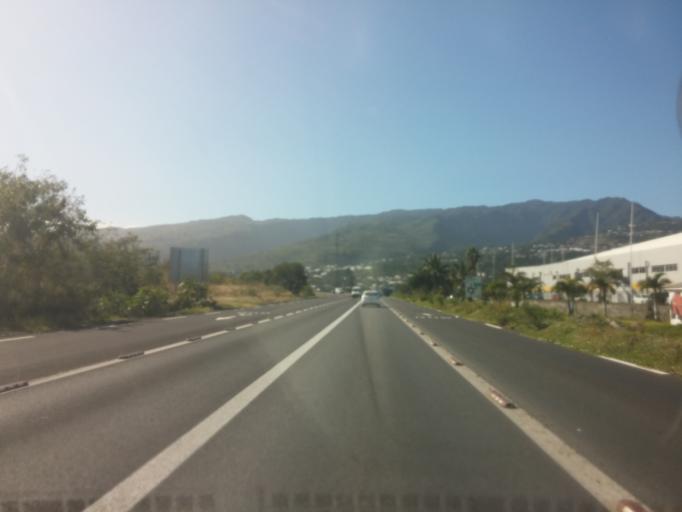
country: RE
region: Reunion
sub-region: Reunion
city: La Possession
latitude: -20.9452
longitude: 55.3207
